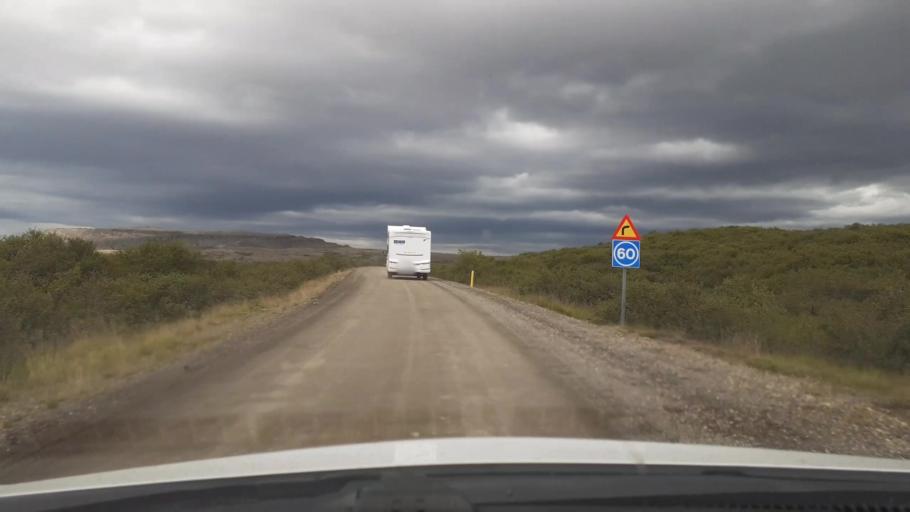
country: IS
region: West
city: Borgarnes
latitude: 64.5515
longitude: -21.6216
